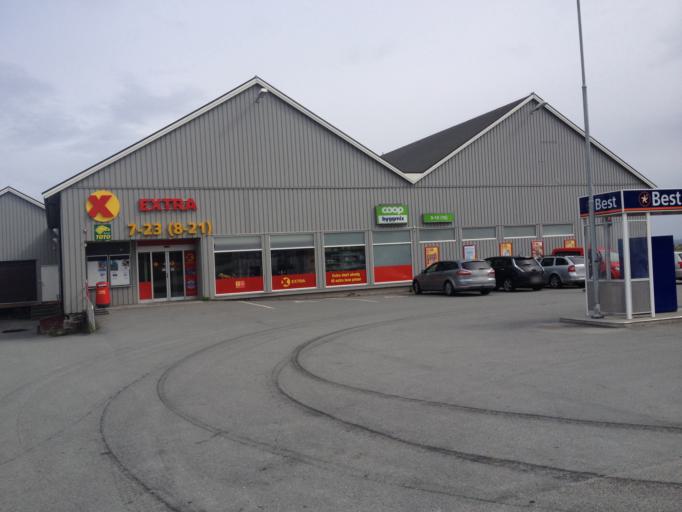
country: NO
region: Sor-Trondelag
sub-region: Froya
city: Sistranda
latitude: 63.7357
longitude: 8.8330
